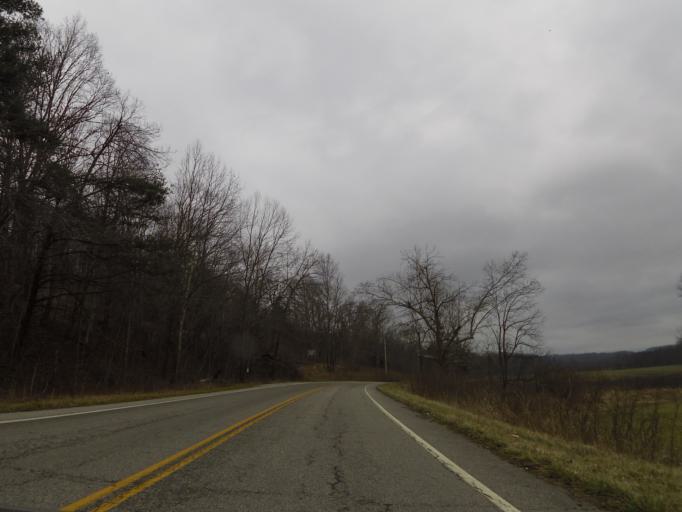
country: US
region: Tennessee
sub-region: Scott County
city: Huntsville
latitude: 36.3204
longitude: -84.6216
